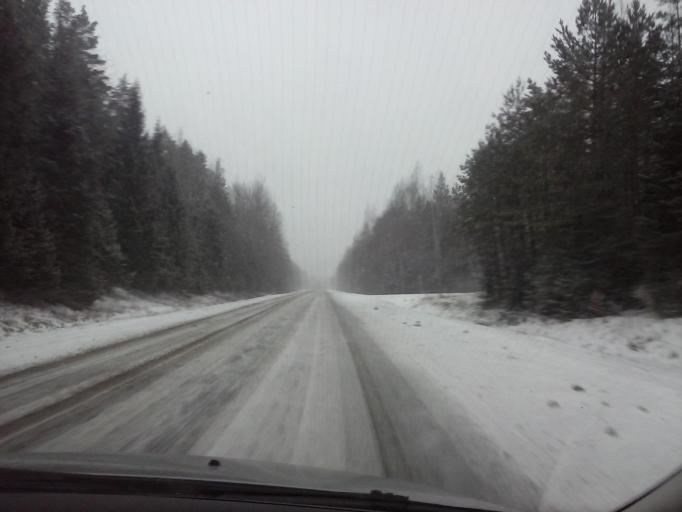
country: LV
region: Valkas Rajons
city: Valka
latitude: 57.7233
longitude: 25.9352
